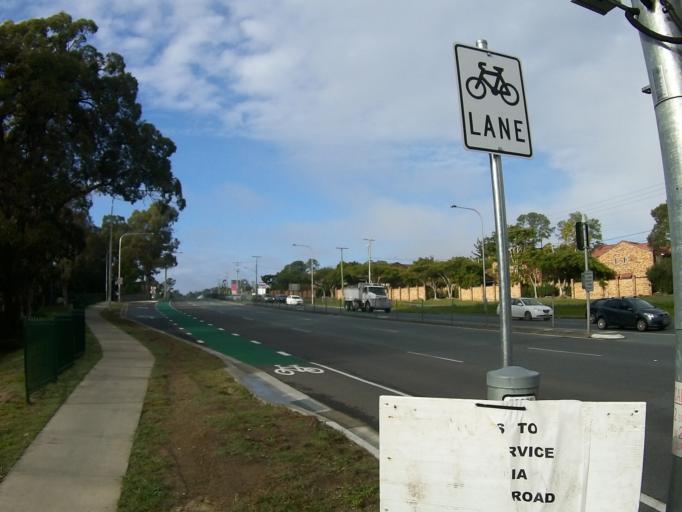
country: AU
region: Queensland
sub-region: Brisbane
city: Upper Mount Gravatt
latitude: -27.5715
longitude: 153.0904
